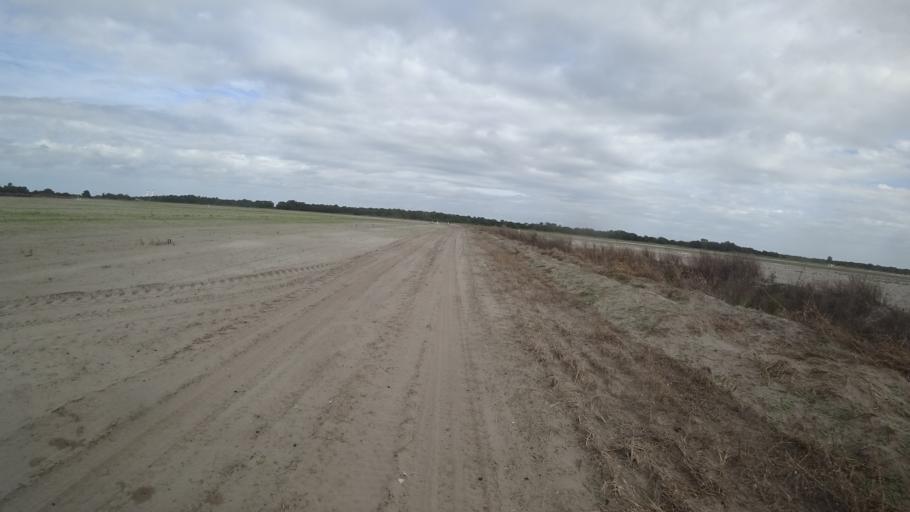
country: US
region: Florida
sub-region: Hillsborough County
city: Wimauma
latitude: 27.5643
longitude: -82.3061
